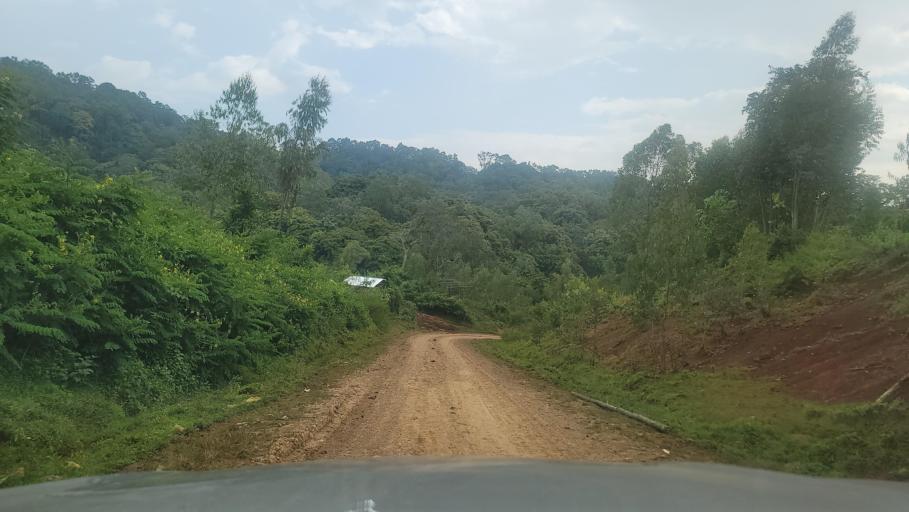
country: ET
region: Southern Nations, Nationalities, and People's Region
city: Bonga
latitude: 7.6896
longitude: 36.2437
